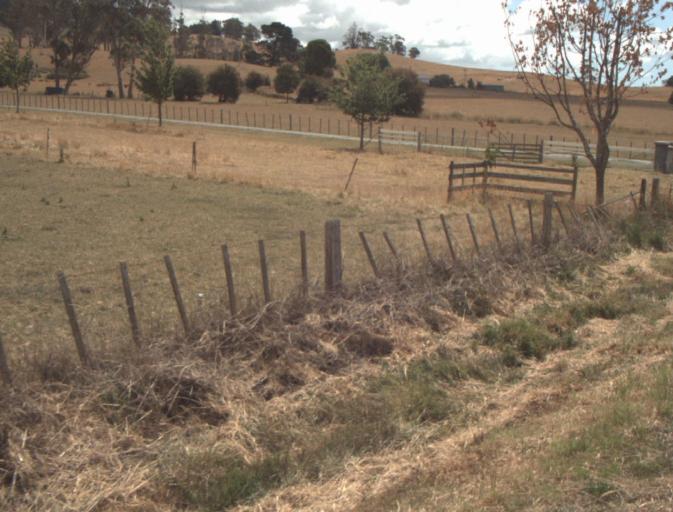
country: AU
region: Tasmania
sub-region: Launceston
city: Mayfield
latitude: -41.2329
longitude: 147.1253
